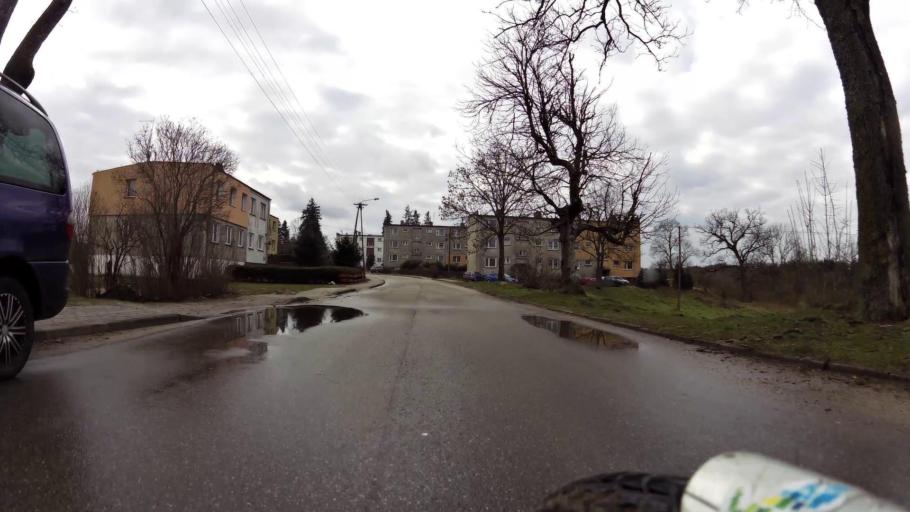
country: PL
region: Pomeranian Voivodeship
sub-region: Powiat bytowski
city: Kolczyglowy
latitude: 54.2392
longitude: 17.2423
